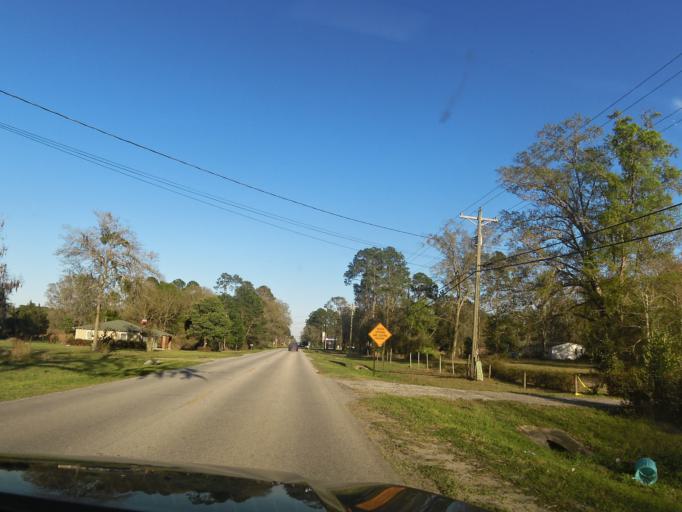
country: US
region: Florida
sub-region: Clay County
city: Middleburg
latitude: 30.1140
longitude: -81.8673
